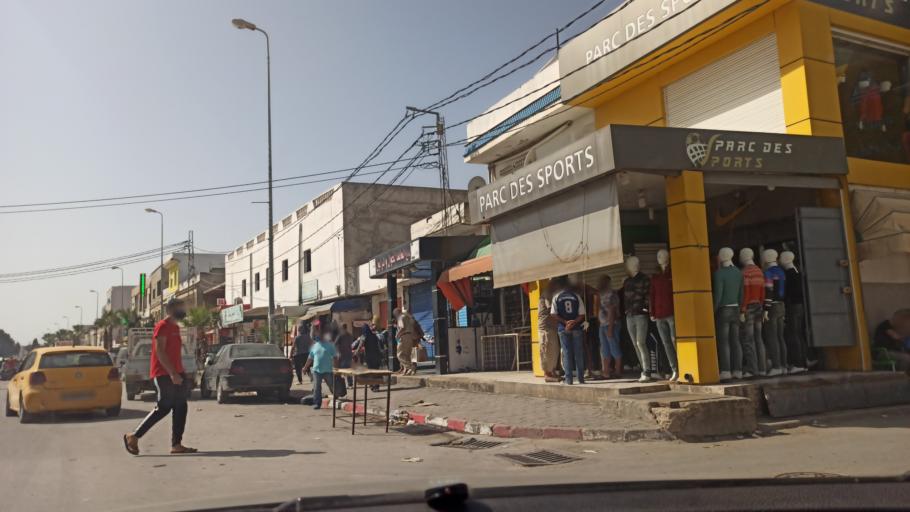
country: TN
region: Manouba
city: Manouba
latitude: 36.7706
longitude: 10.1128
